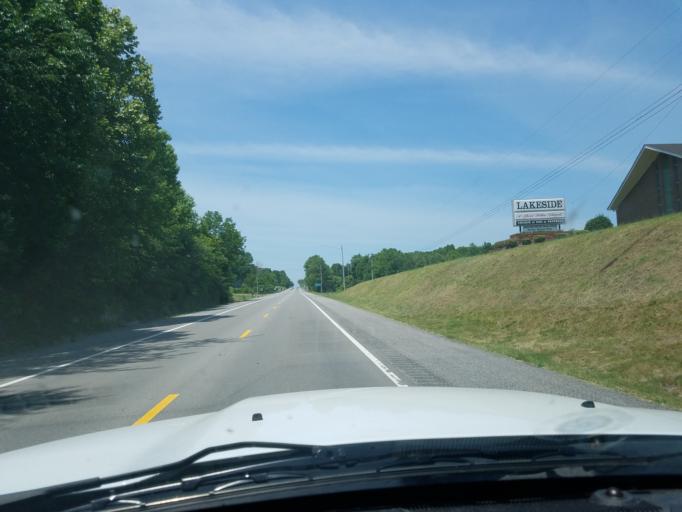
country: US
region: Tennessee
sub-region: Sumner County
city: Westmoreland
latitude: 36.5697
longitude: -86.2397
